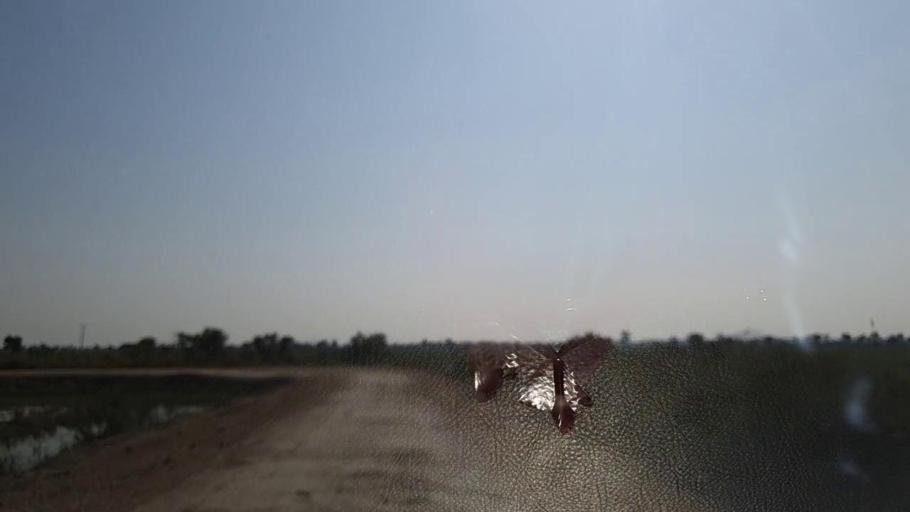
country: PK
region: Sindh
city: Sanghar
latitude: 25.9898
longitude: 69.0605
